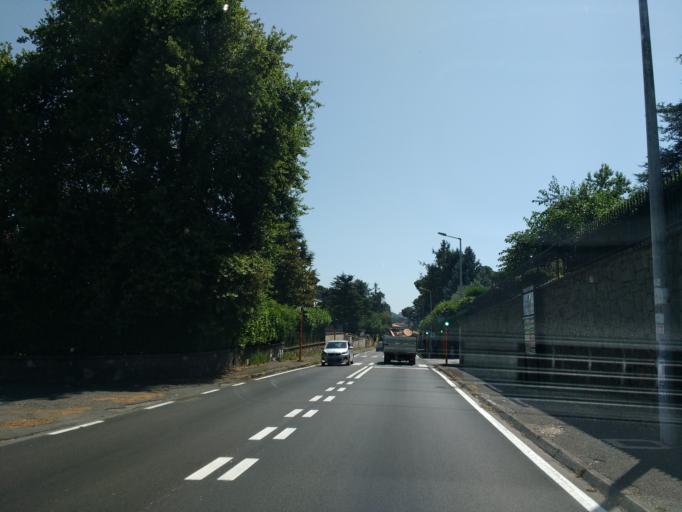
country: IT
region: Latium
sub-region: Citta metropolitana di Roma Capitale
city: Grottaferrata
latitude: 41.7882
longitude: 12.6820
